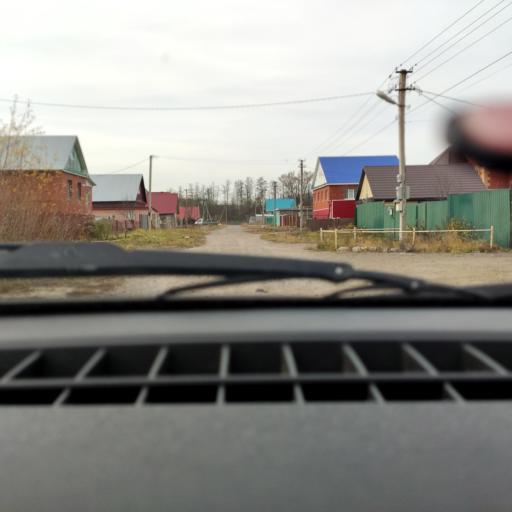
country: RU
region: Bashkortostan
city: Ufa
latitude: 54.8135
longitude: 56.1847
